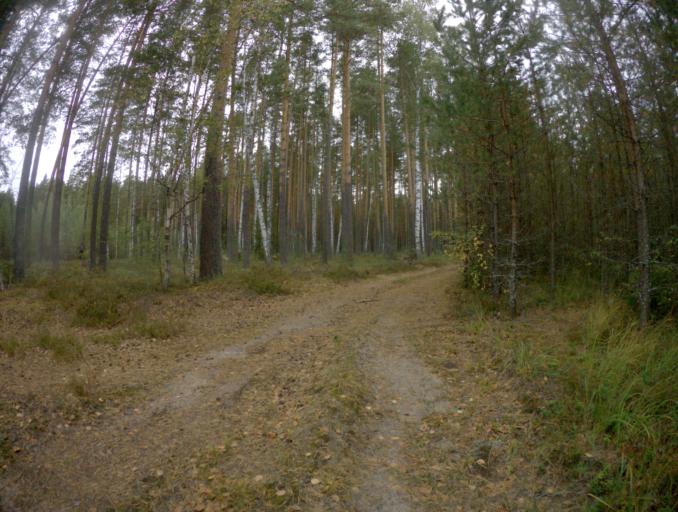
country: RU
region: Vladimir
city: Golovino
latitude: 55.8741
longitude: 40.3960
